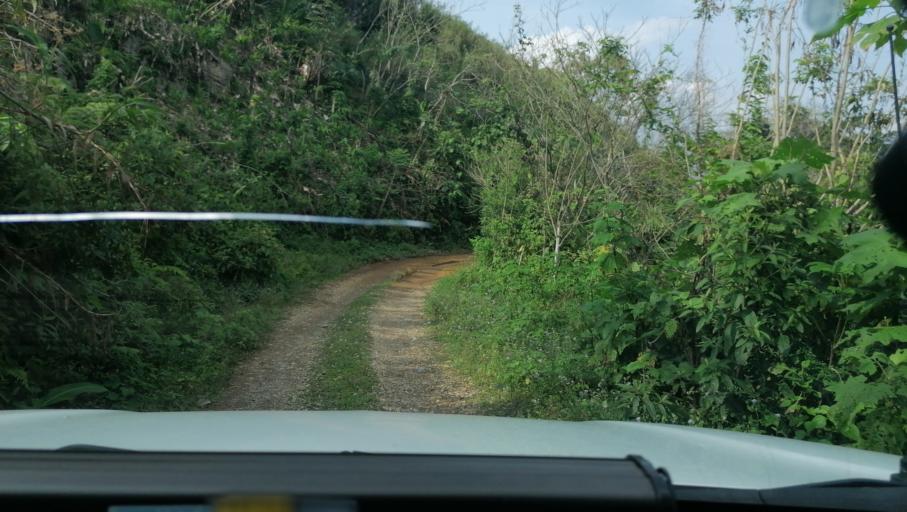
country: MX
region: Chiapas
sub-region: Tapilula
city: San Francisco Jacona
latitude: 17.3086
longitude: -93.1018
